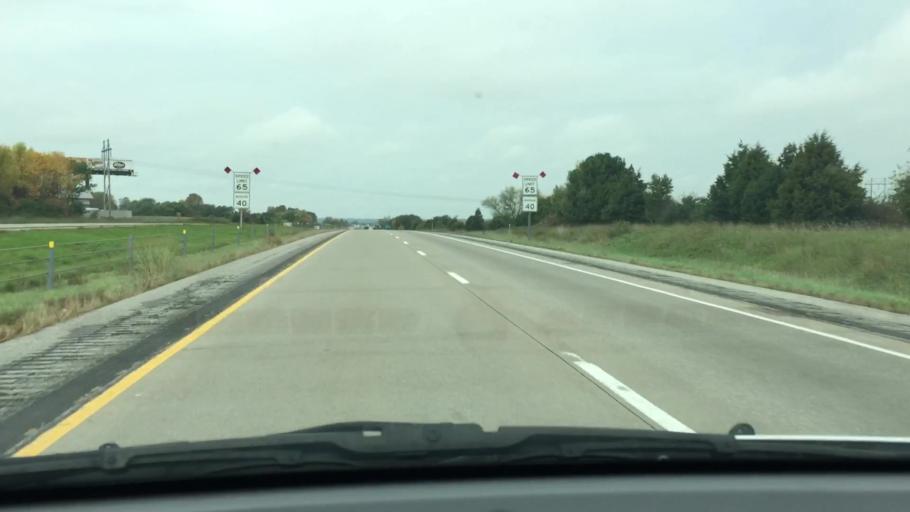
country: US
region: Iowa
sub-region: Johnson County
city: Iowa City
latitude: 41.6755
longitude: -91.4557
